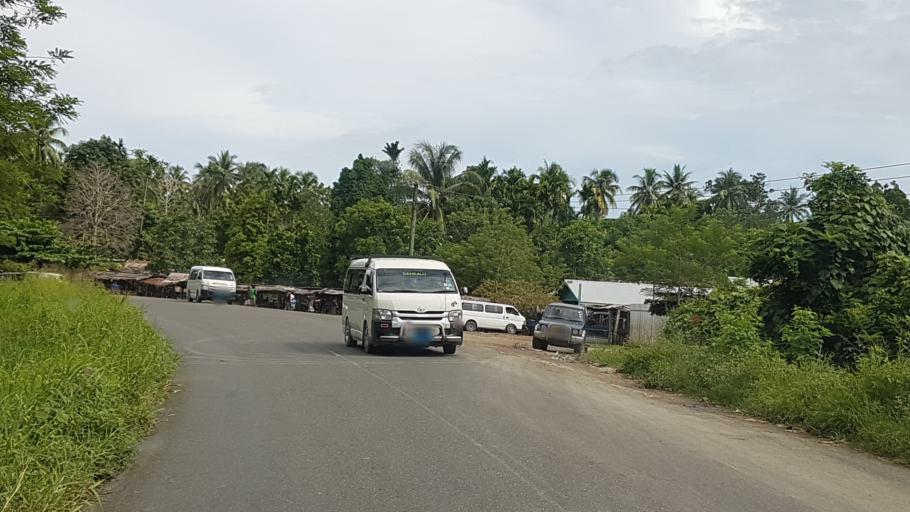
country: PG
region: Madang
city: Madang
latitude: -5.0810
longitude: 145.7778
